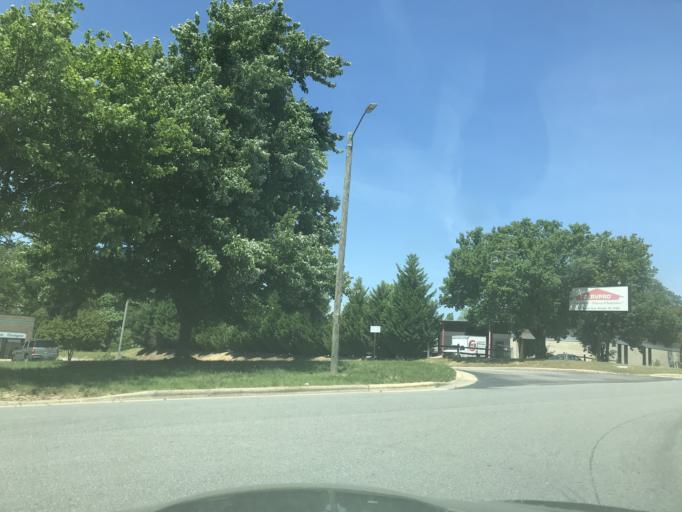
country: US
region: North Carolina
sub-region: Wake County
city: Raleigh
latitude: 35.7978
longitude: -78.5846
